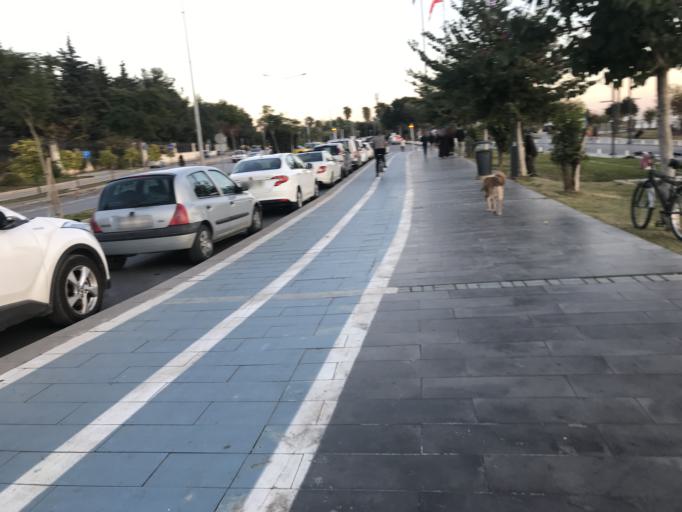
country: TR
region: Antalya
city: Antalya
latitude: 36.8851
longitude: 30.6787
